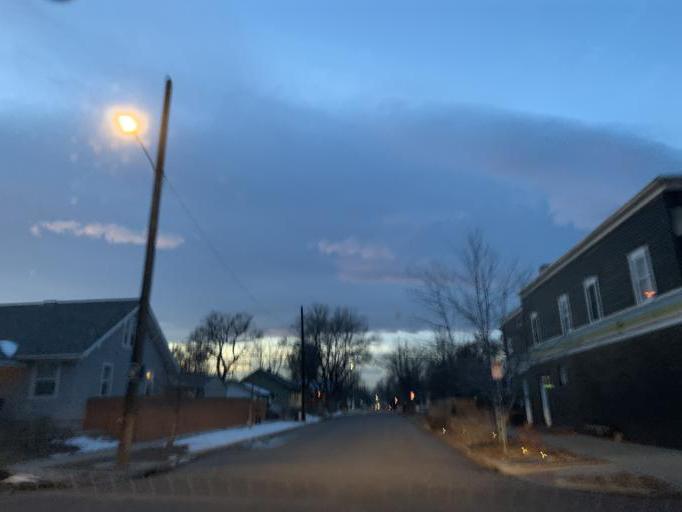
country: US
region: Colorado
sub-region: Jefferson County
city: Edgewater
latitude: 39.7748
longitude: -105.0508
